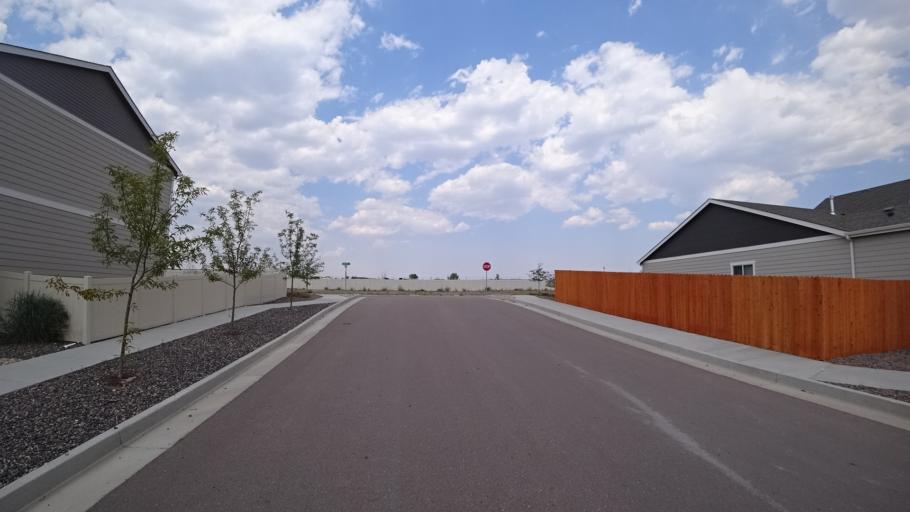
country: US
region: Colorado
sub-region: El Paso County
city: Black Forest
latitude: 38.9477
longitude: -104.6868
